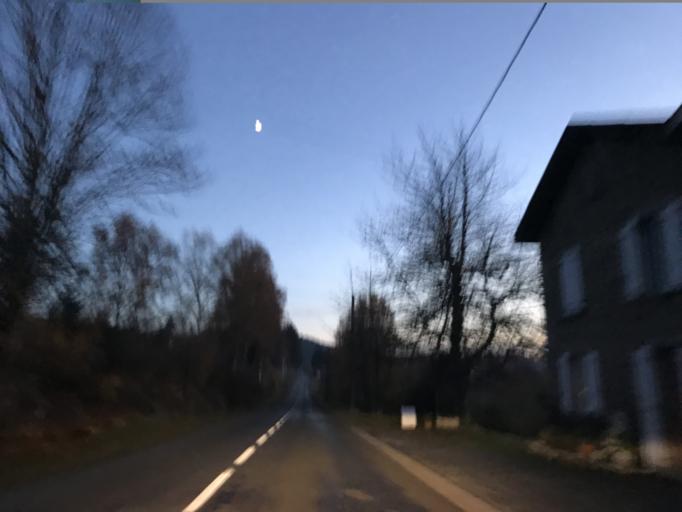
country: FR
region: Auvergne
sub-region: Departement du Puy-de-Dome
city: Celles-sur-Durolle
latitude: 45.7802
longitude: 3.6795
